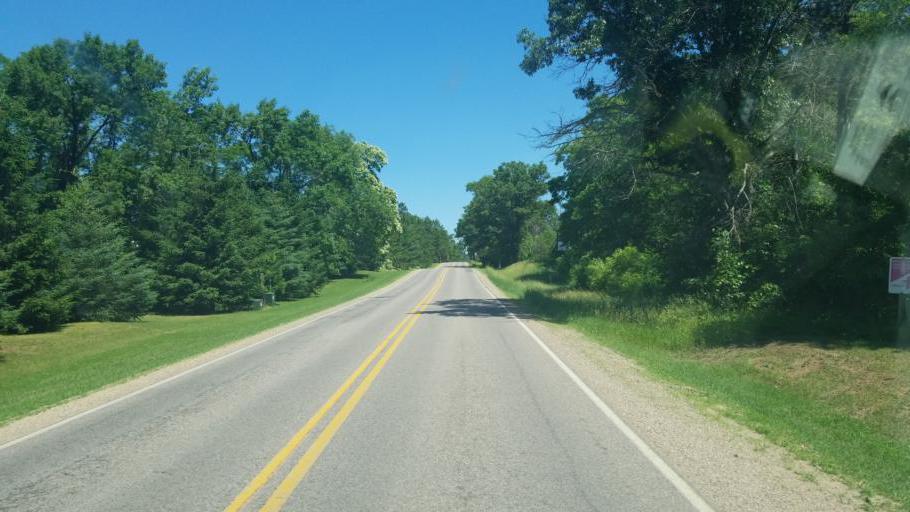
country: US
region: Wisconsin
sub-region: Adams County
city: Adams
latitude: 43.9085
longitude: -89.9377
